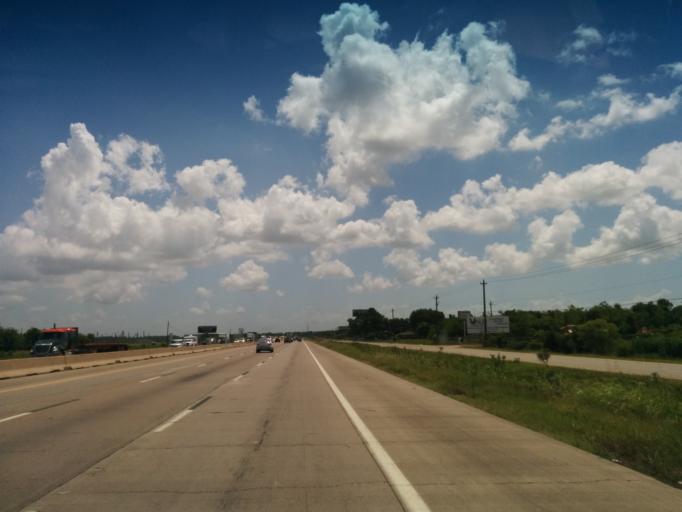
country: US
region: Texas
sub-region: Chambers County
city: Mont Belvieu
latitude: 29.8098
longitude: -94.9519
